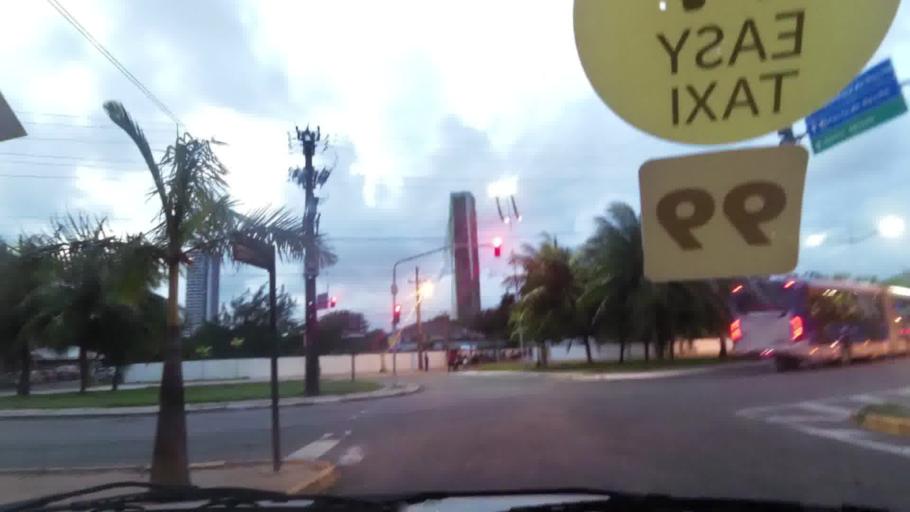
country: BR
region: Pernambuco
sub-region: Recife
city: Recife
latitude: -8.0536
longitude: -34.8715
